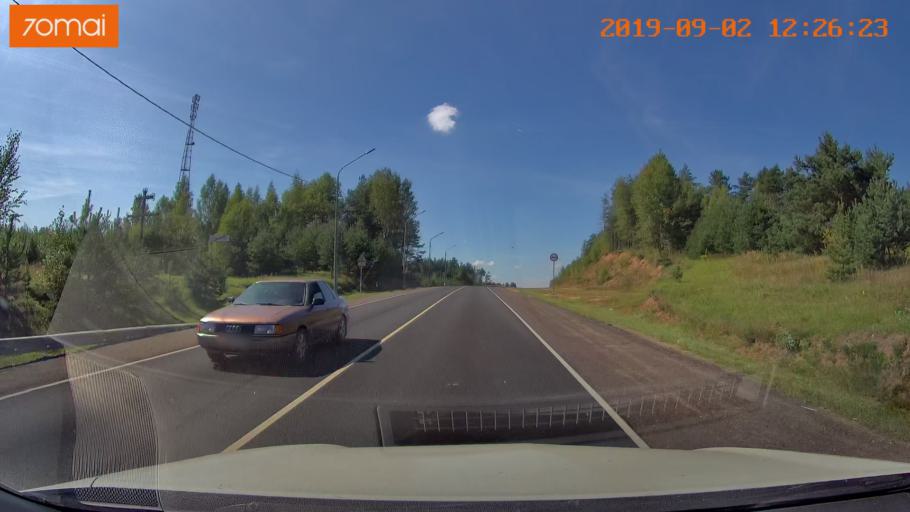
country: RU
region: Smolensk
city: Shumyachi
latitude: 53.8570
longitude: 32.5672
